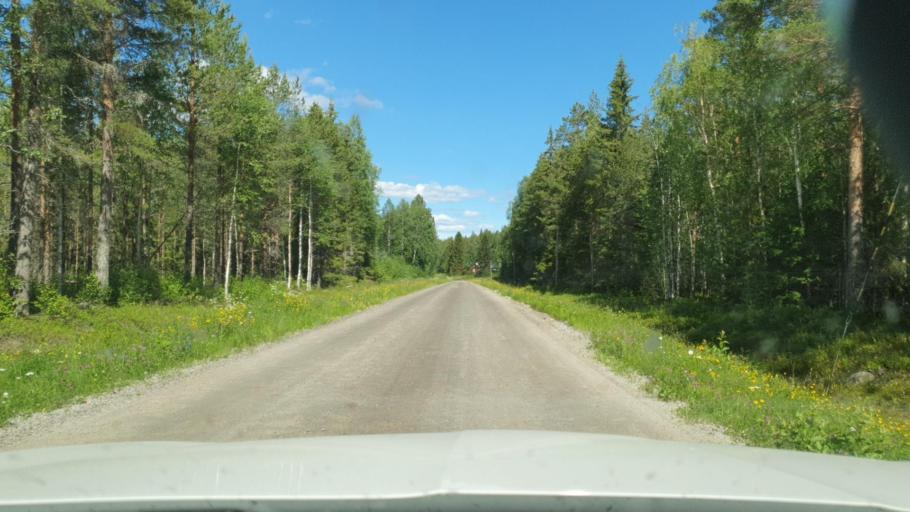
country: SE
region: Vaesterbotten
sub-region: Skelleftea Kommun
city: Backa
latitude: 65.1536
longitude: 21.1604
